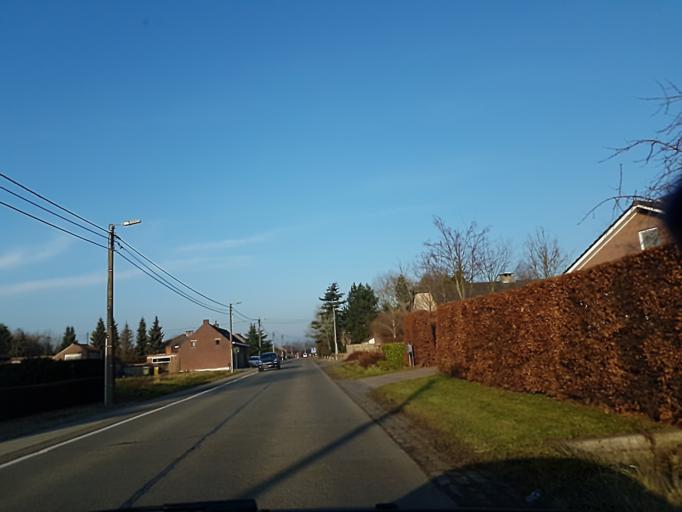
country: BE
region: Flanders
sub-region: Provincie Vlaams-Brabant
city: Tremelo
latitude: 51.0328
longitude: 4.7113
